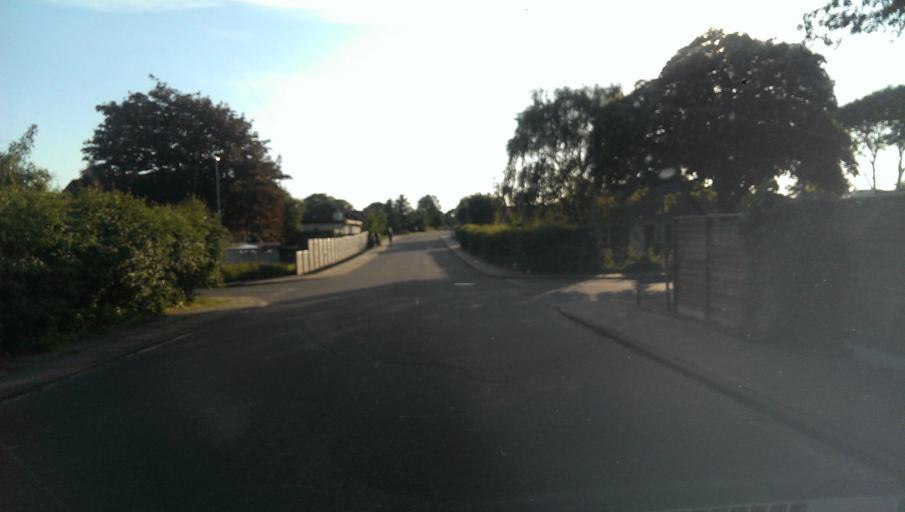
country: DK
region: South Denmark
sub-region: Esbjerg Kommune
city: Esbjerg
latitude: 55.5021
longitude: 8.4472
